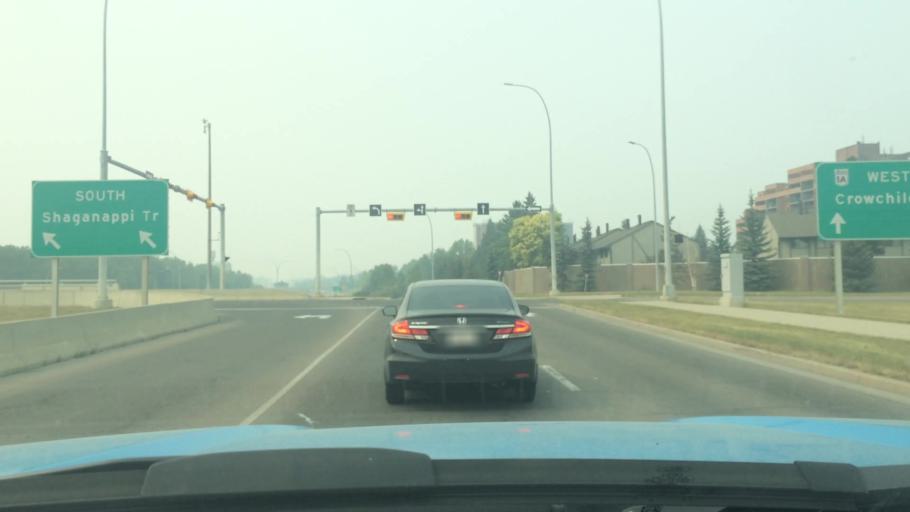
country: CA
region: Alberta
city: Calgary
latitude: 51.0985
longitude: -114.1489
